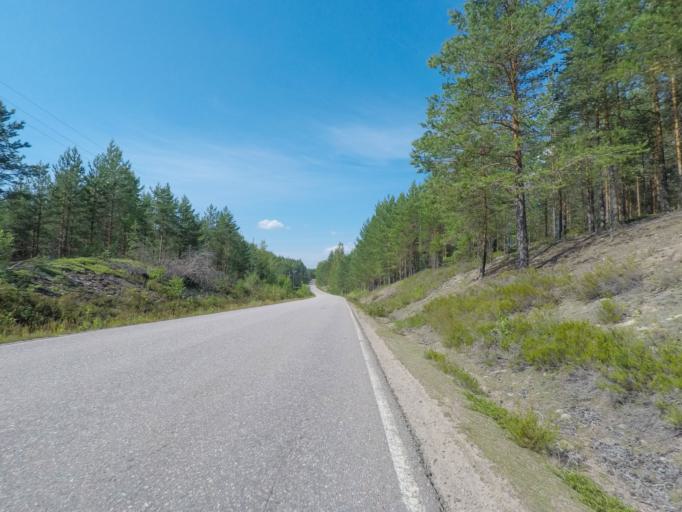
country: FI
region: Southern Savonia
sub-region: Mikkeli
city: Puumala
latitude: 61.4613
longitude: 28.1754
